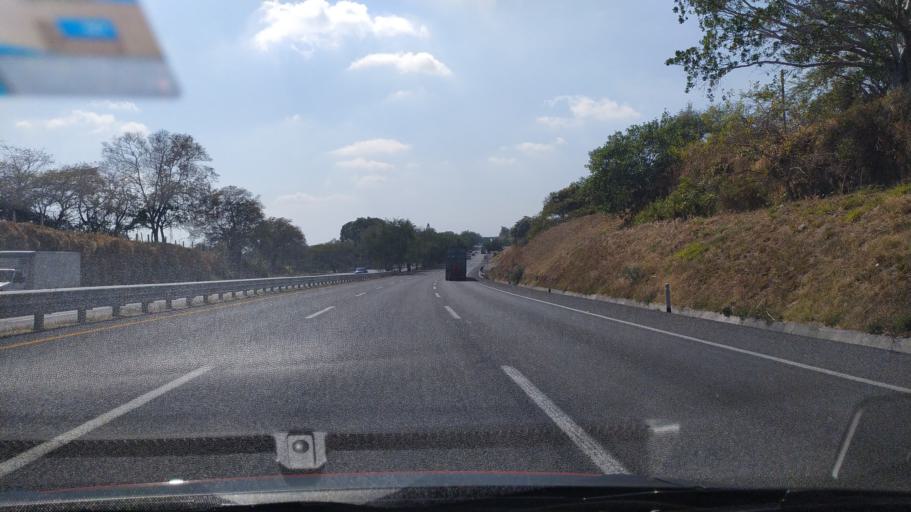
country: MX
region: Colima
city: Cuauhtemoc
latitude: 19.3074
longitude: -103.6119
